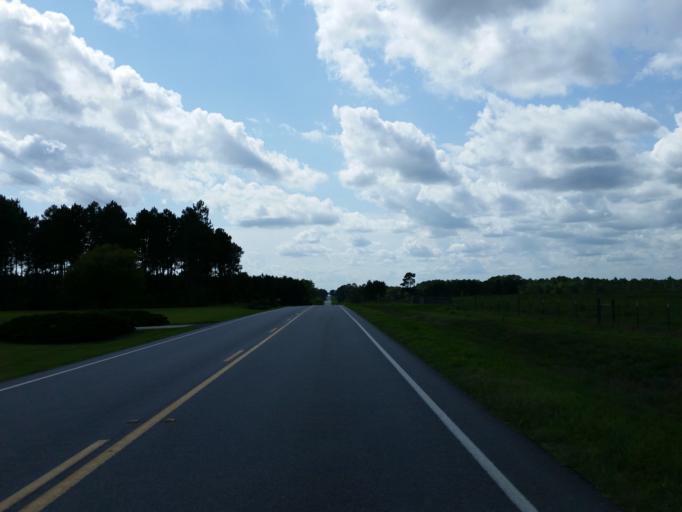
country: US
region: Georgia
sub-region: Turner County
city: Ashburn
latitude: 31.6429
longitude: -83.5304
